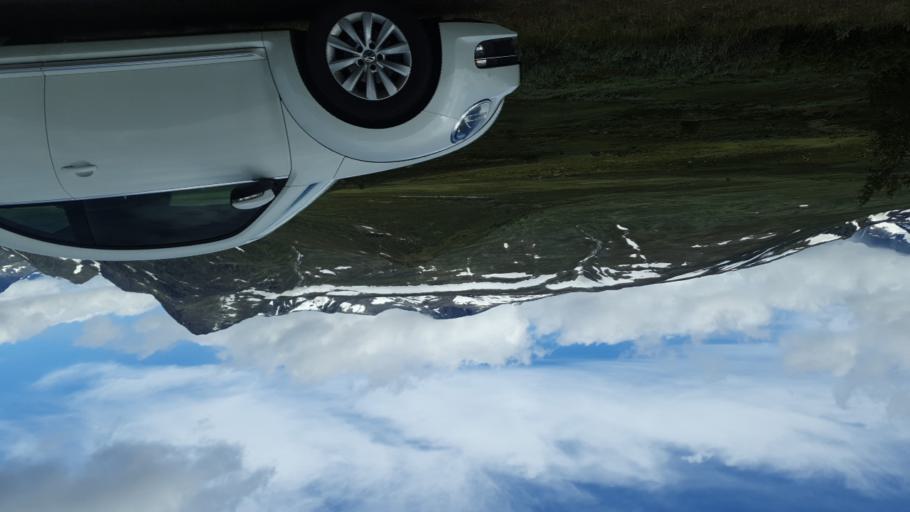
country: NO
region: Oppland
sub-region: Vang
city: Vang
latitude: 61.4548
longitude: 8.8061
